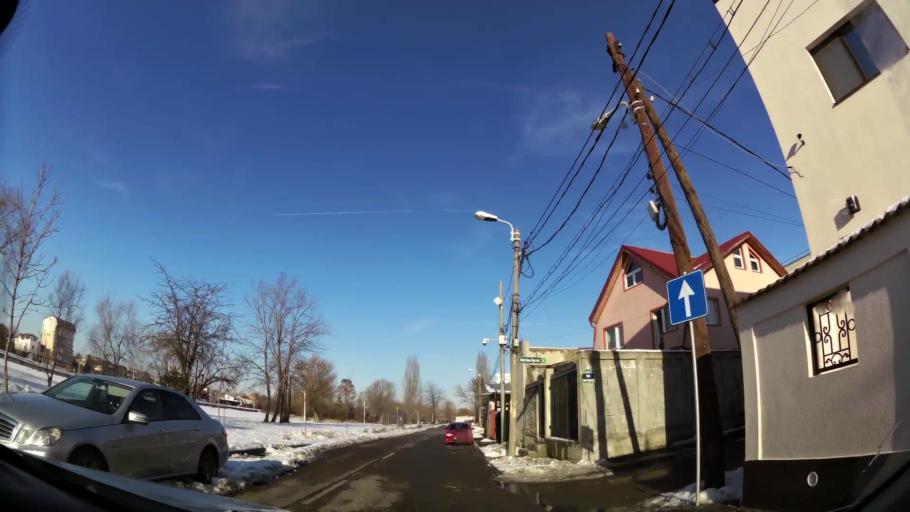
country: RO
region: Ilfov
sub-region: Comuna Fundeni-Dobroesti
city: Fundeni
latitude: 44.4699
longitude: 26.1315
